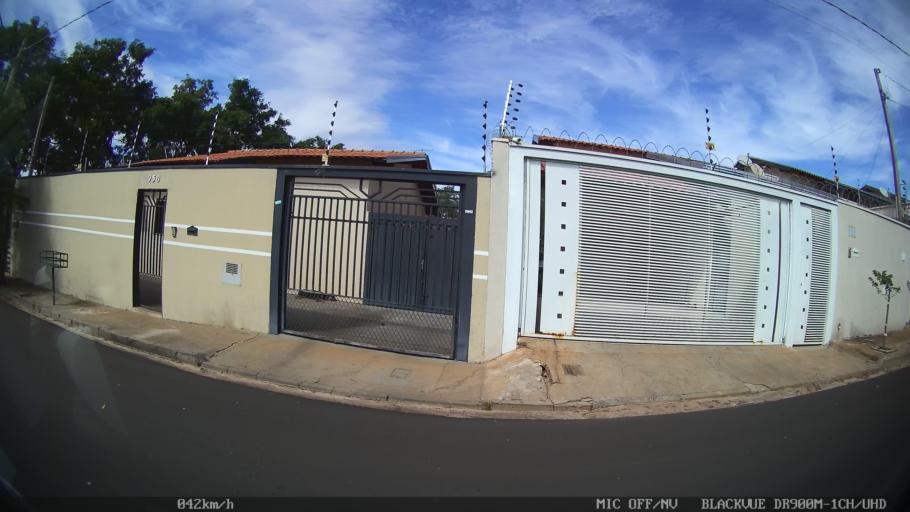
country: BR
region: Sao Paulo
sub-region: Sao Jose Do Rio Preto
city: Sao Jose do Rio Preto
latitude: -20.8324
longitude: -49.3481
